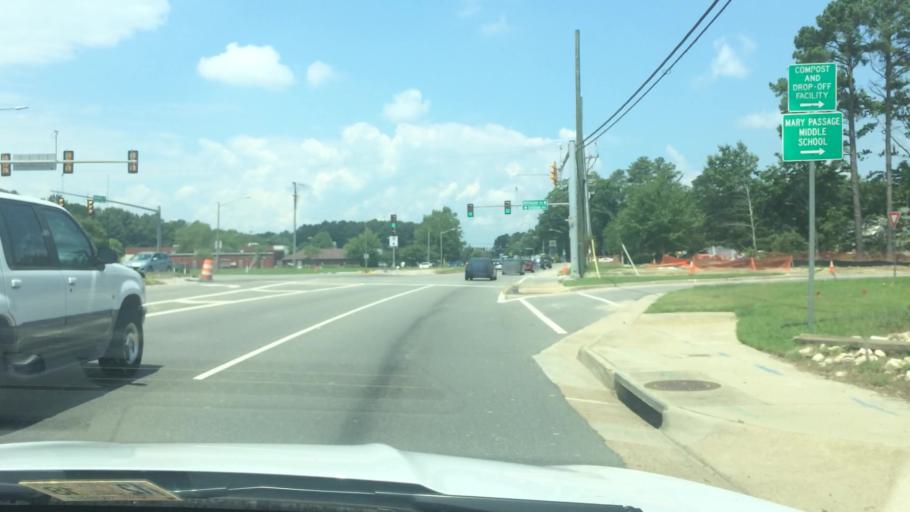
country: US
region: Virginia
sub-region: York County
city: Yorktown
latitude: 37.1485
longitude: -76.5524
